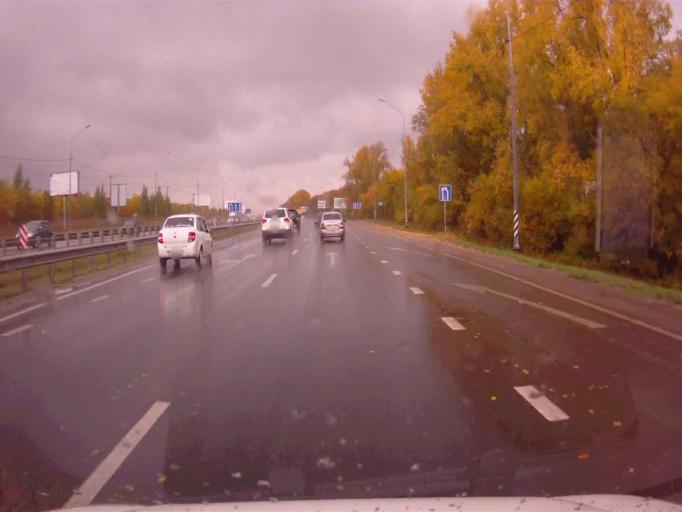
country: RU
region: Chelyabinsk
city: Dolgoderevenskoye
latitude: 55.2839
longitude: 61.3429
